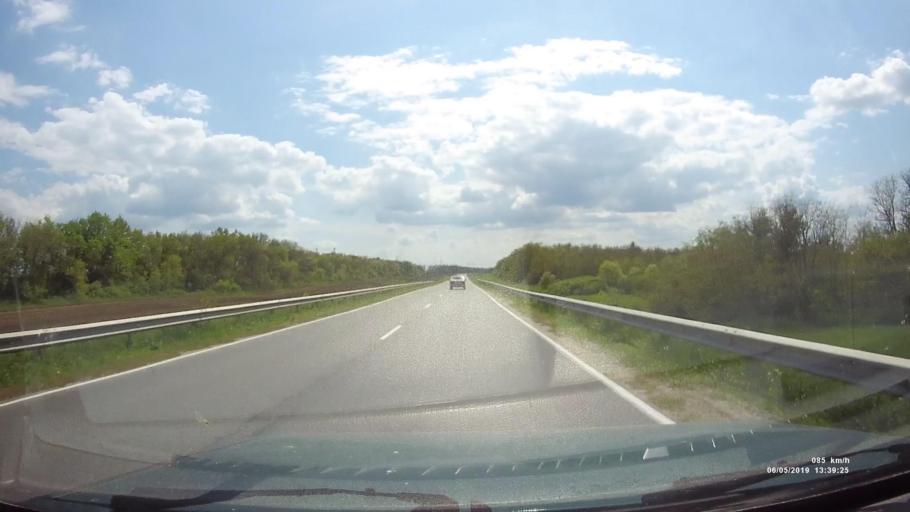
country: RU
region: Rostov
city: Ust'-Donetskiy
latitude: 47.6756
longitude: 40.7029
